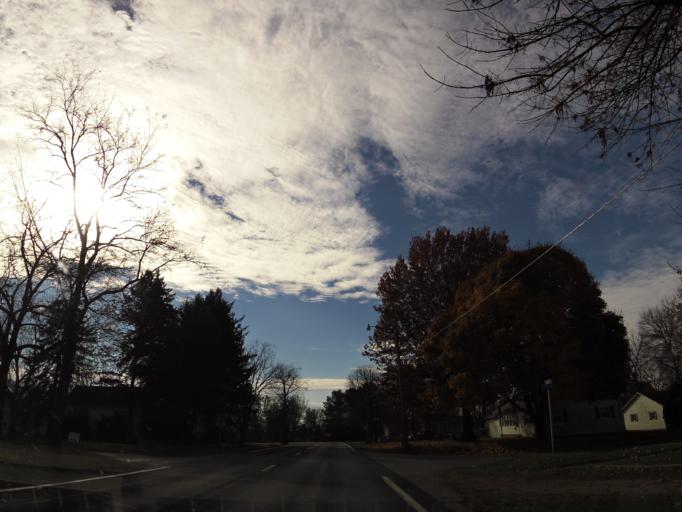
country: US
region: Illinois
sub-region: De Witt County
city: Farmer City
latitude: 40.2461
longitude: -88.6356
